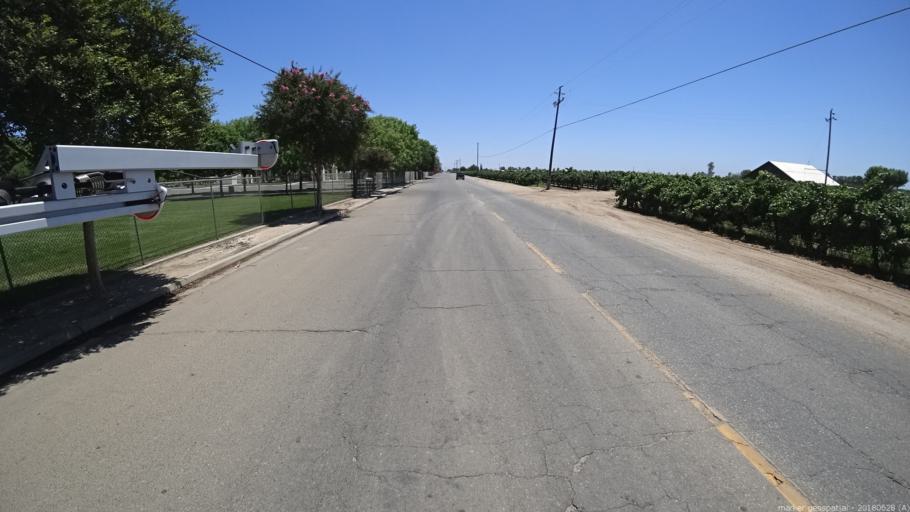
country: US
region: California
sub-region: Madera County
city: Parksdale
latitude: 36.9526
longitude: -120.0328
